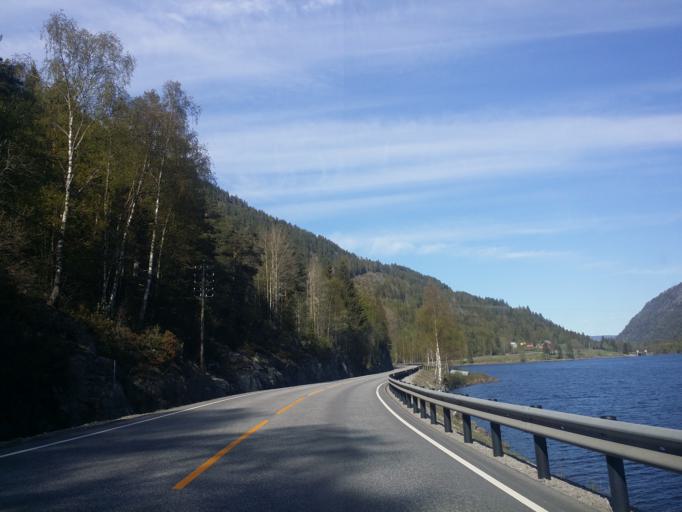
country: NO
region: Telemark
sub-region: Seljord
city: Seljord
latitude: 59.6072
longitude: 8.7445
